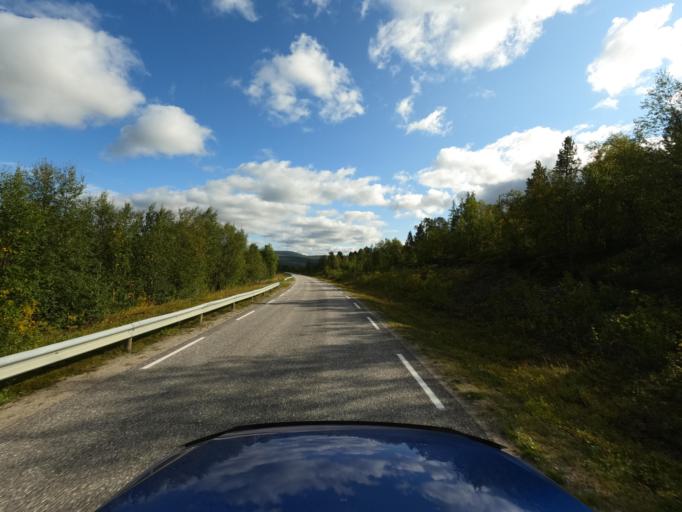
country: NO
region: Finnmark Fylke
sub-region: Karasjok
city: Karasjohka
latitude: 69.4330
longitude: 25.7196
